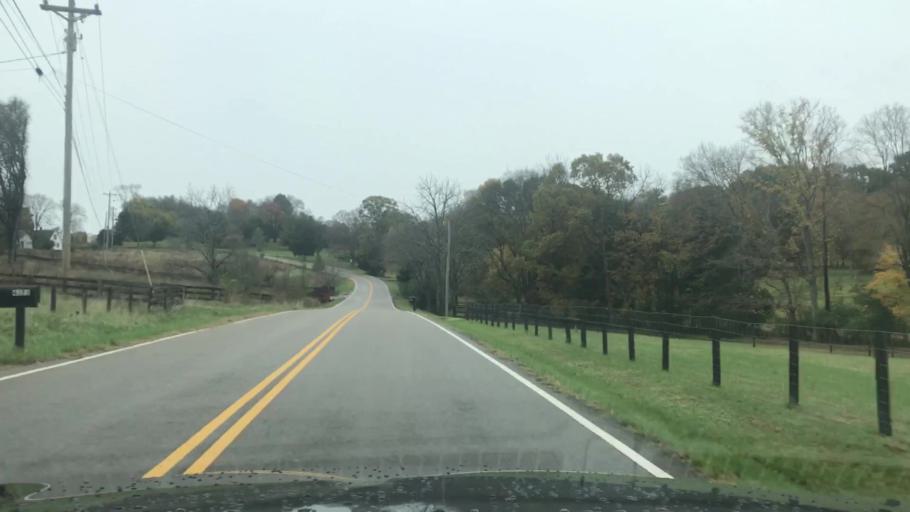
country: US
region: Tennessee
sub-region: Williamson County
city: Franklin
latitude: 35.8924
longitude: -86.8170
